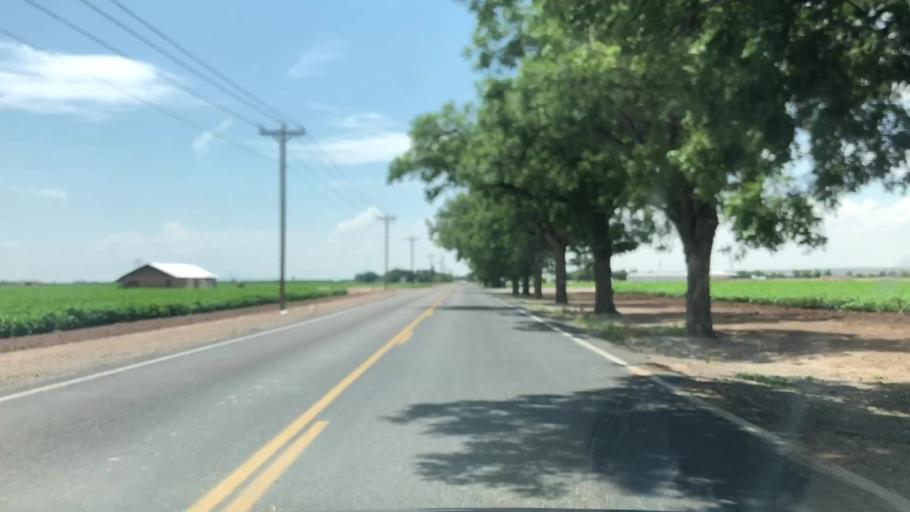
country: US
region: New Mexico
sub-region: Dona Ana County
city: Vado
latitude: 32.1038
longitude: -106.6836
